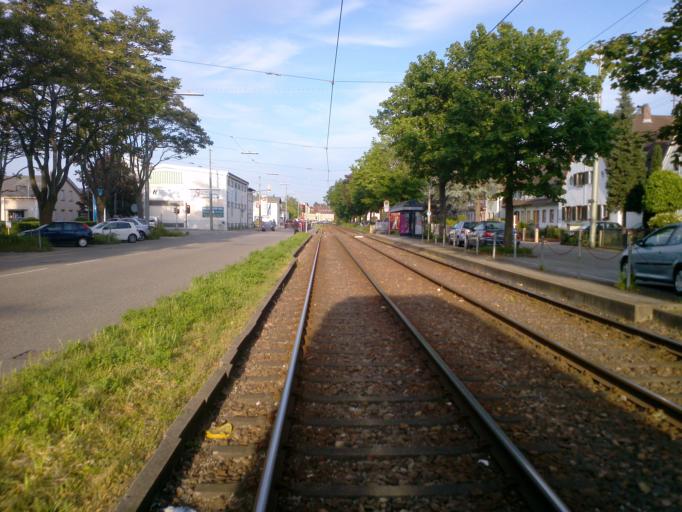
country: DE
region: Baden-Wuerttemberg
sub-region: Karlsruhe Region
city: Rheinstetten
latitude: 49.0073
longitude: 8.3431
